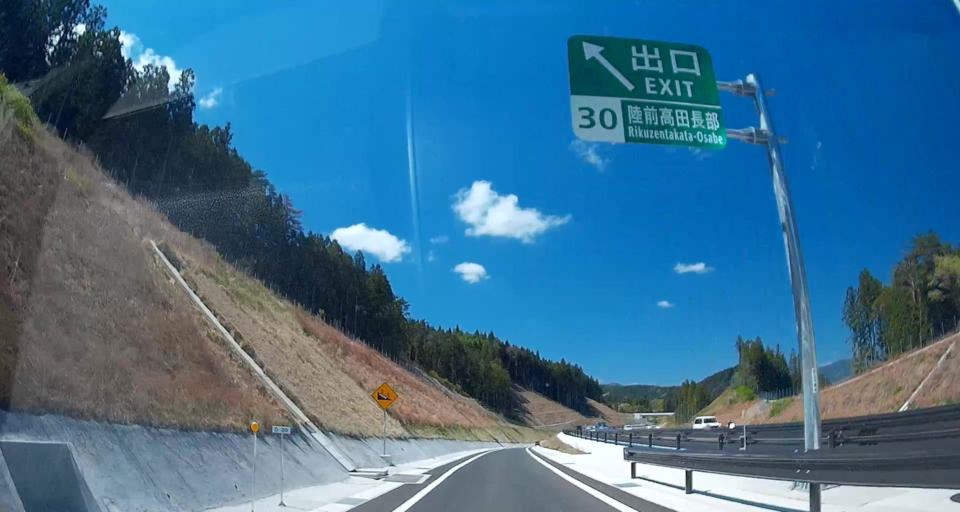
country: JP
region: Iwate
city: Ofunato
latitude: 38.9833
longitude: 141.6143
